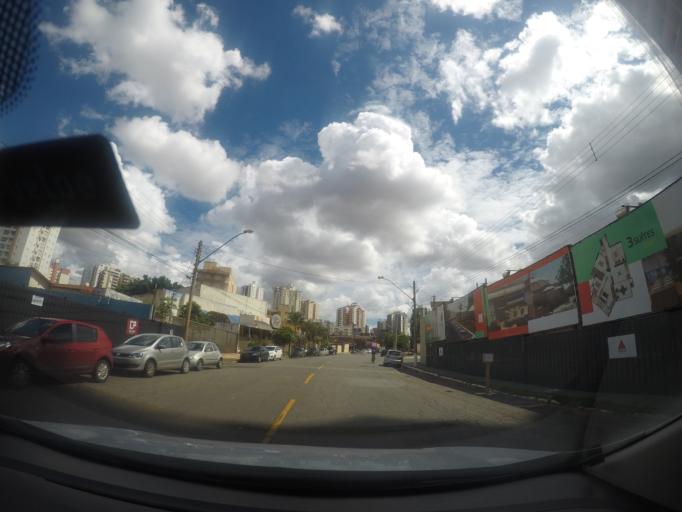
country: BR
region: Goias
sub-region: Goiania
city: Goiania
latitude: -16.6850
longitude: -49.2775
